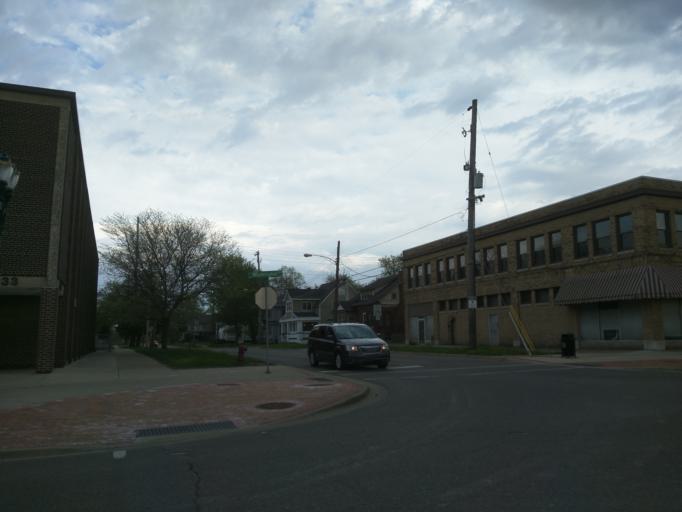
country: US
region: Michigan
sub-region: Ingham County
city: Lansing
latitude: 42.7220
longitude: -84.5523
